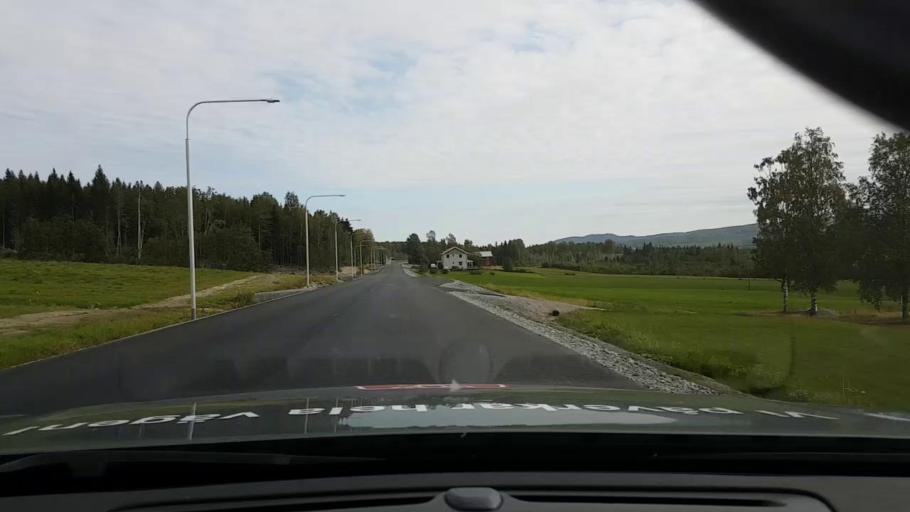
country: SE
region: Vaesternorrland
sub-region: OErnskoeldsviks Kommun
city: Bjasta
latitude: 63.2931
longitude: 18.4788
